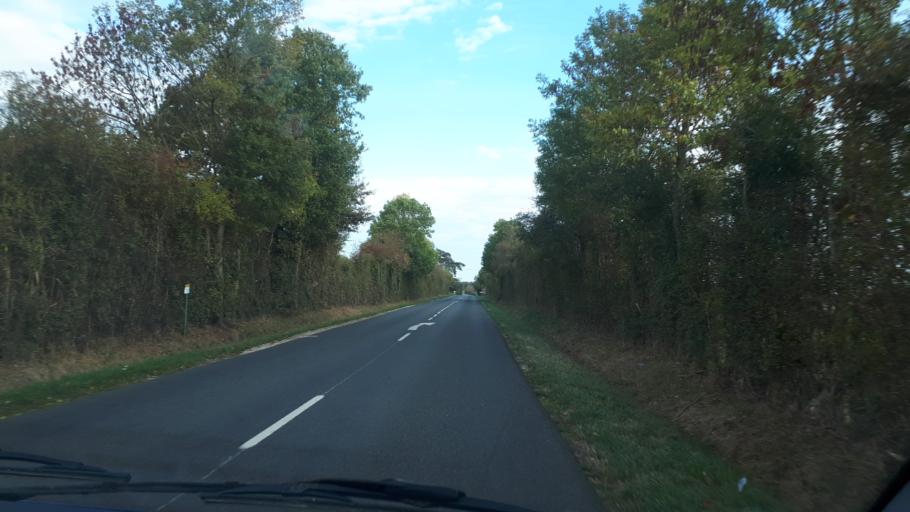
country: FR
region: Centre
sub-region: Departement du Loir-et-Cher
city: Mondoubleau
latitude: 47.9273
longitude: 0.9330
